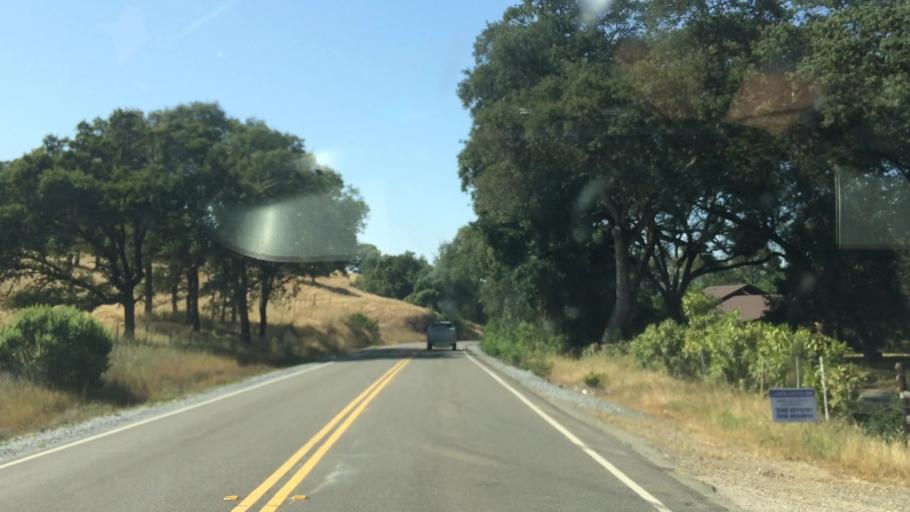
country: US
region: California
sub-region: Amador County
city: Plymouth
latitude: 38.5096
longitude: -120.9475
